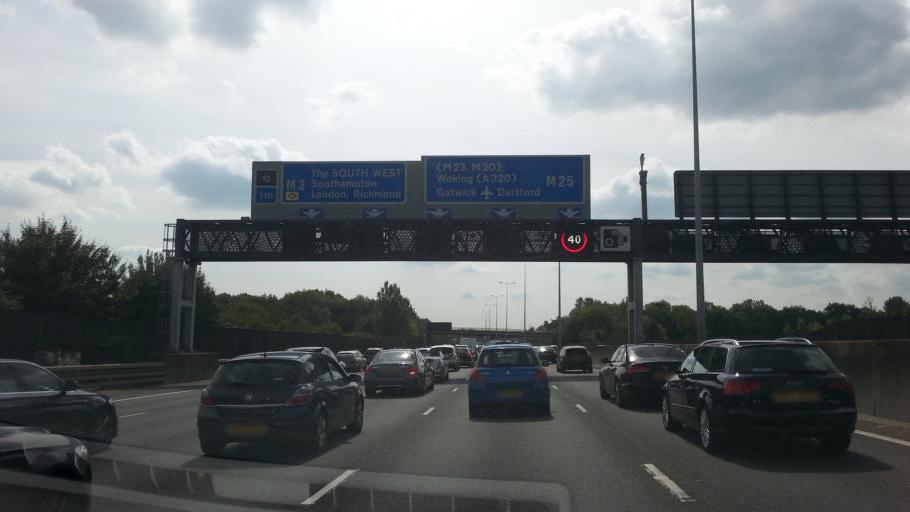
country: GB
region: England
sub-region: Surrey
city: Egham
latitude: 51.4262
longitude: -0.5407
